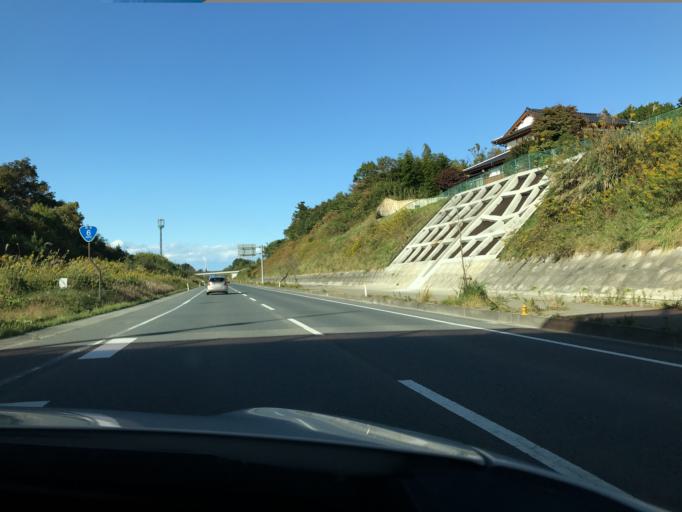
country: JP
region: Miyagi
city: Marumori
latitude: 37.8098
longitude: 140.9434
